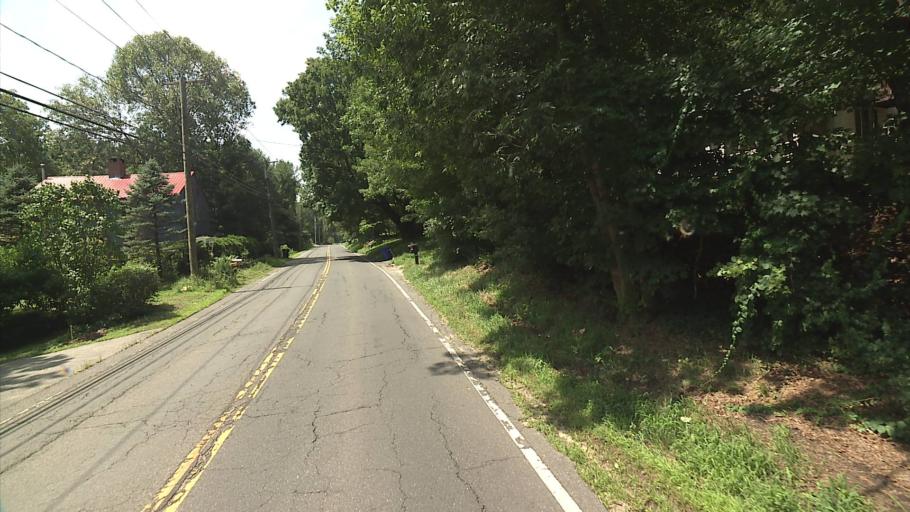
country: US
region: Connecticut
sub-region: Tolland County
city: South Coventry
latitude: 41.7618
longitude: -72.2802
